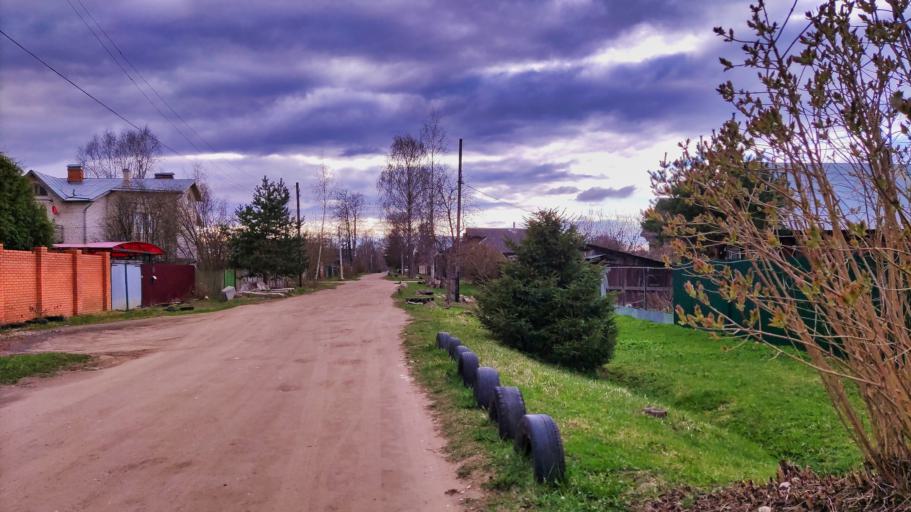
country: RU
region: Tverskaya
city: Rzhev
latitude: 56.2505
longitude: 34.3407
